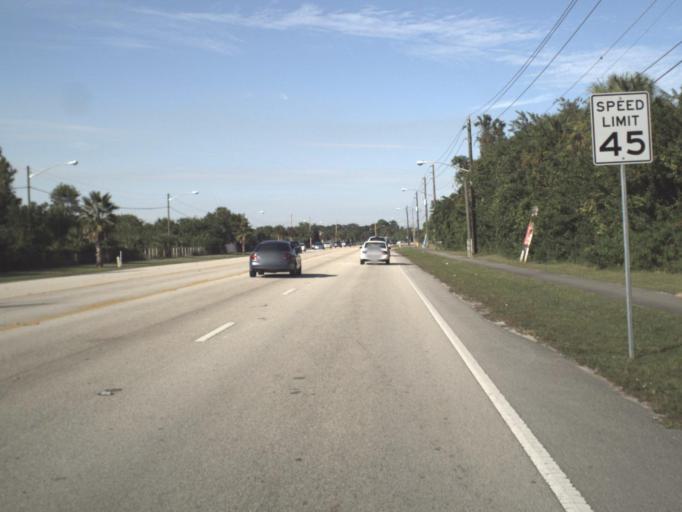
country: US
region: Florida
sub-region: Brevard County
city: June Park
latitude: 28.0008
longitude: -80.6725
